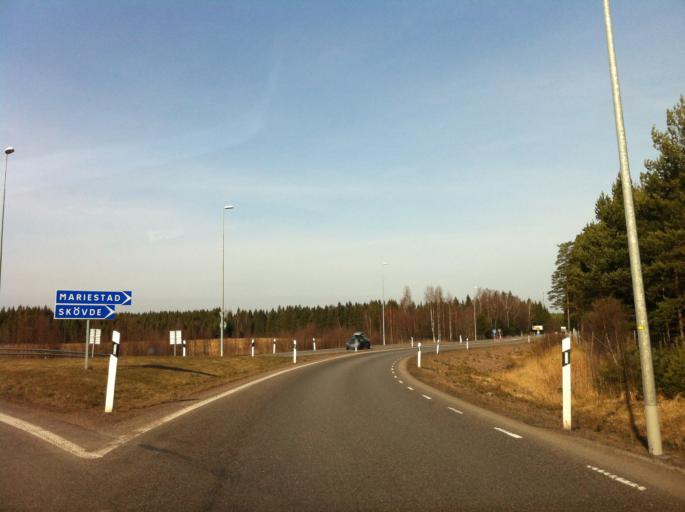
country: SE
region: Vaestra Goetaland
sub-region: Tidaholms Kommun
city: Tidaholm
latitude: 58.1391
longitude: 13.8970
